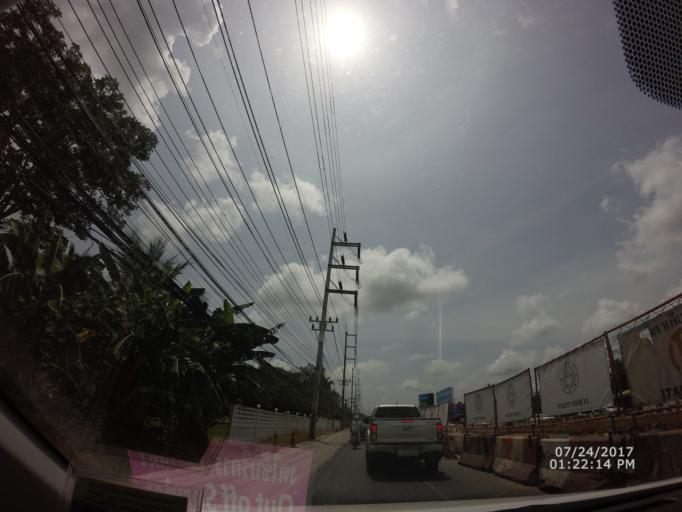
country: TH
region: Phuket
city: Thalang
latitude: 8.0911
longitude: 98.3396
